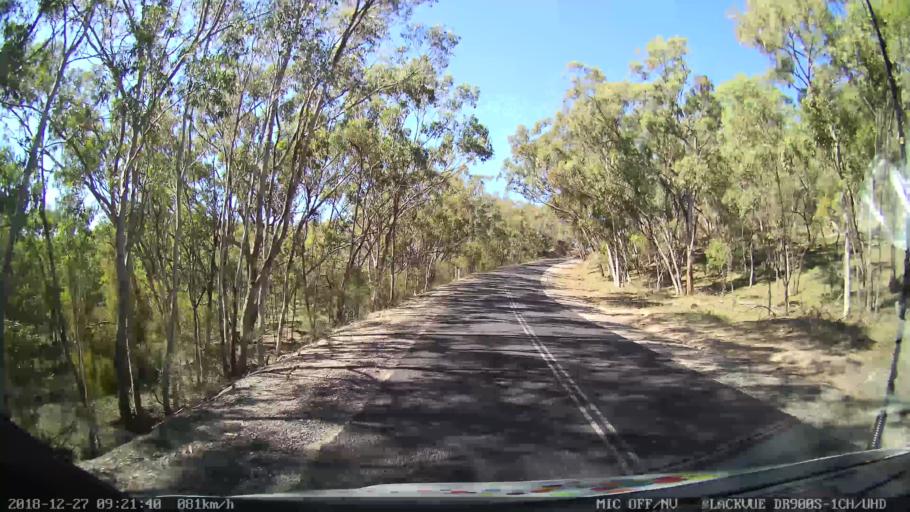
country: AU
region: New South Wales
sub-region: Lithgow
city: Portland
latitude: -33.1262
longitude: 150.0156
